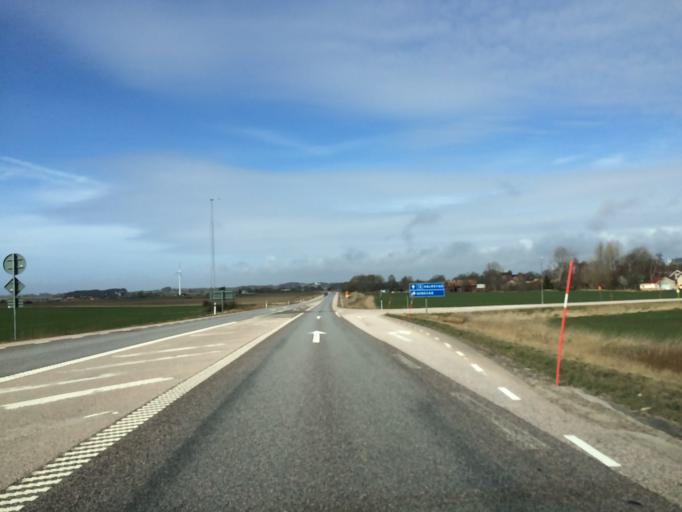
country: SE
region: Halland
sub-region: Laholms Kommun
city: Veinge
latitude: 56.5631
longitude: 13.0291
